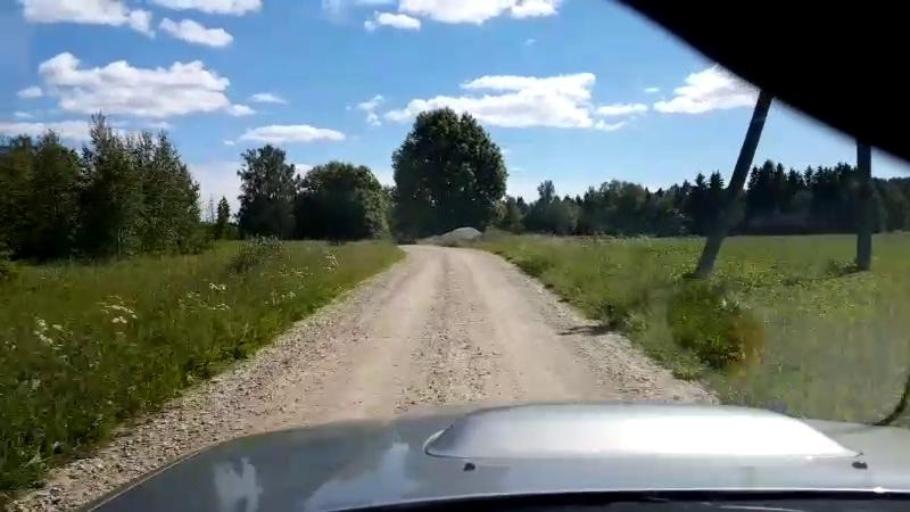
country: EE
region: Paernumaa
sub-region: Halinga vald
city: Parnu-Jaagupi
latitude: 58.5348
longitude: 24.5446
